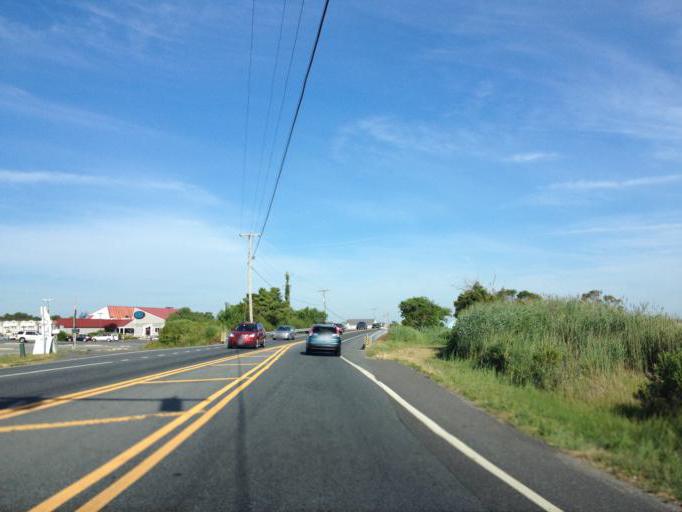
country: US
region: Delaware
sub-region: Sussex County
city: Bethany Beach
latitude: 38.4521
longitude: -75.0617
